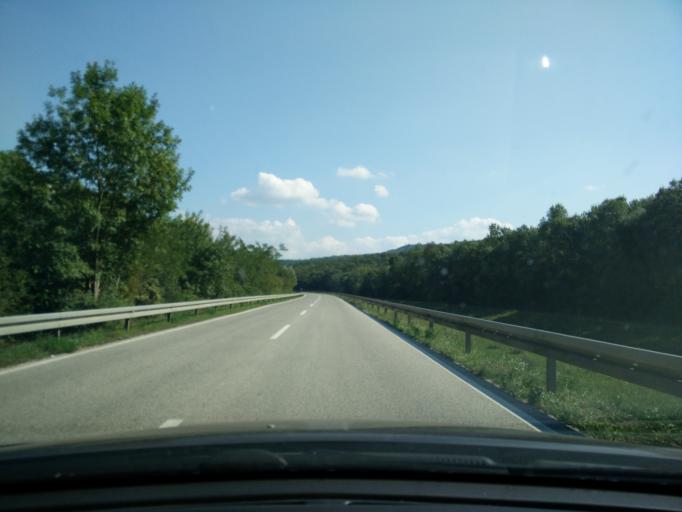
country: HR
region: Istarska
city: Buje
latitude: 45.3556
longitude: 13.7425
